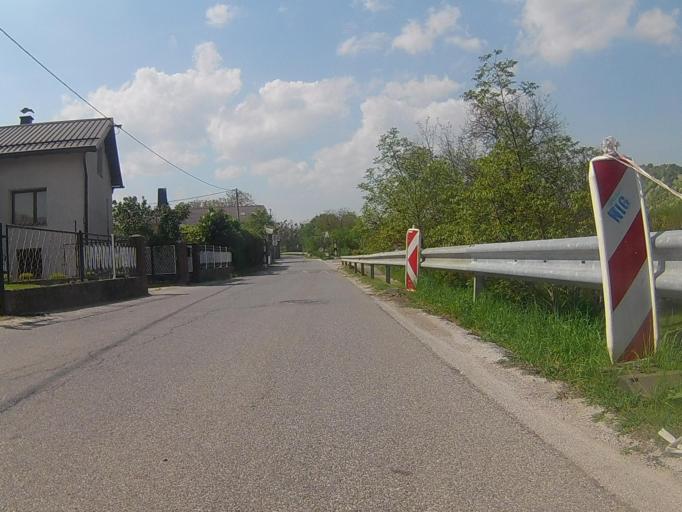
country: SI
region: Maribor
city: Maribor
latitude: 46.5520
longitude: 15.6829
